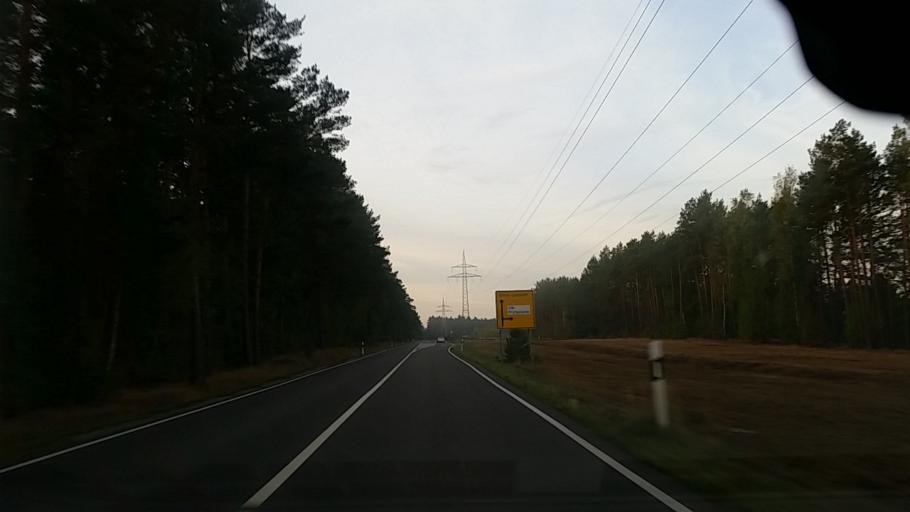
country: DE
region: Lower Saxony
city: Bergfeld
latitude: 52.5976
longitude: 10.7988
